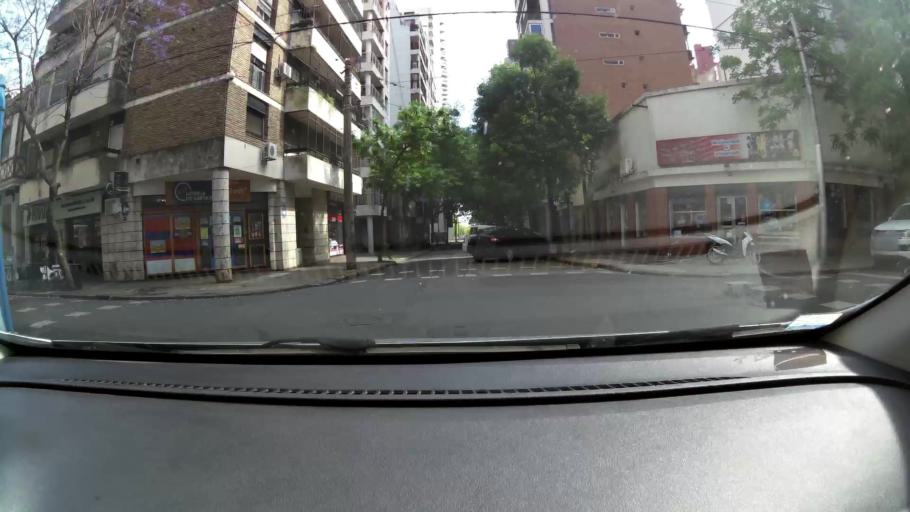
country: AR
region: Santa Fe
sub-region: Departamento de Rosario
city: Rosario
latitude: -32.9551
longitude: -60.6257
